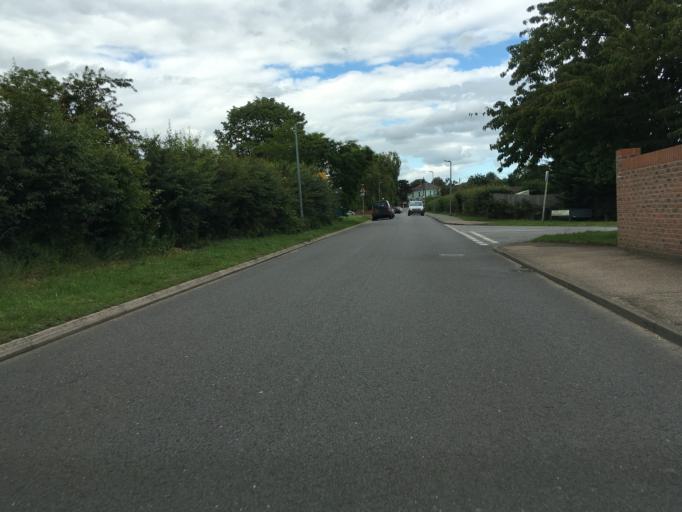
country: GB
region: England
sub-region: Central Bedfordshire
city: Leighton Buzzard
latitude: 51.9446
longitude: -0.6596
